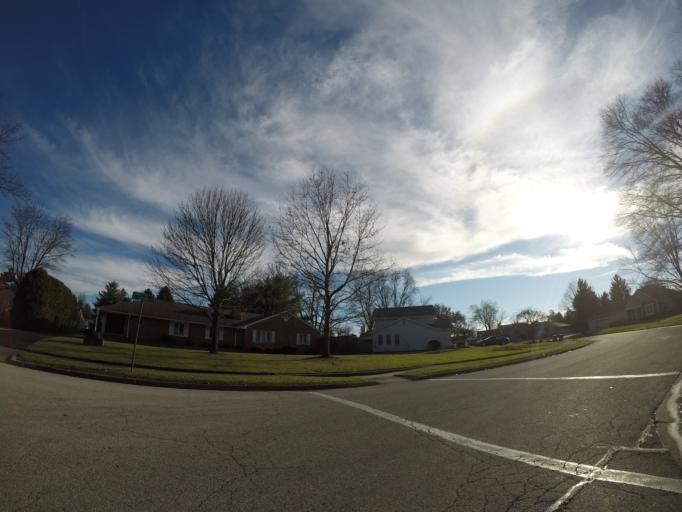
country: US
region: Ohio
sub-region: Franklin County
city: Upper Arlington
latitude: 40.0279
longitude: -83.0566
